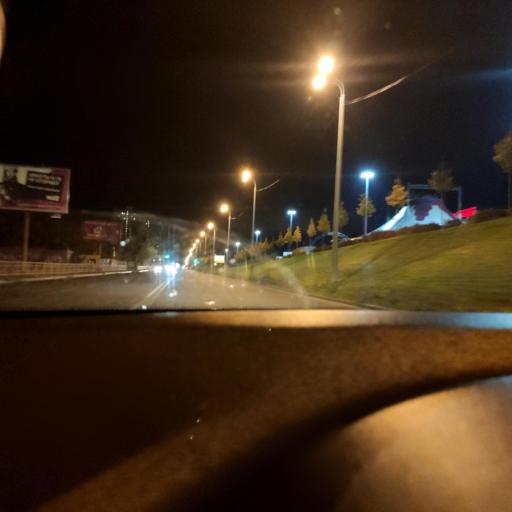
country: RU
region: Samara
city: Samara
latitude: 53.2062
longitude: 50.2027
